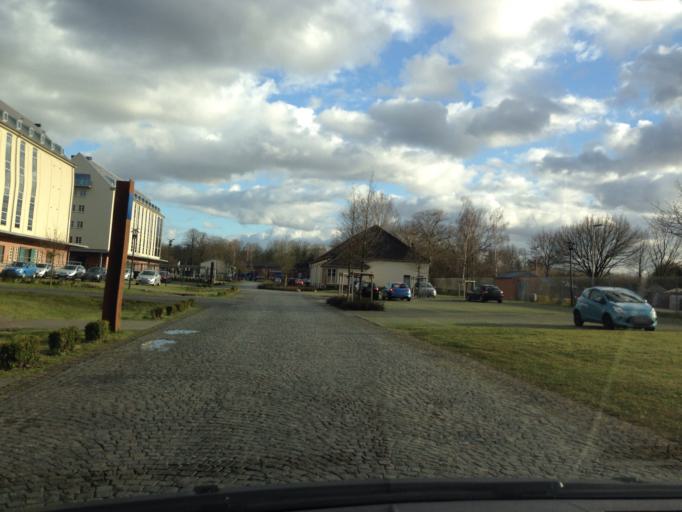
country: DE
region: North Rhine-Westphalia
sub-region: Regierungsbezirk Munster
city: Muenster
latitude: 51.9984
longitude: 7.6338
